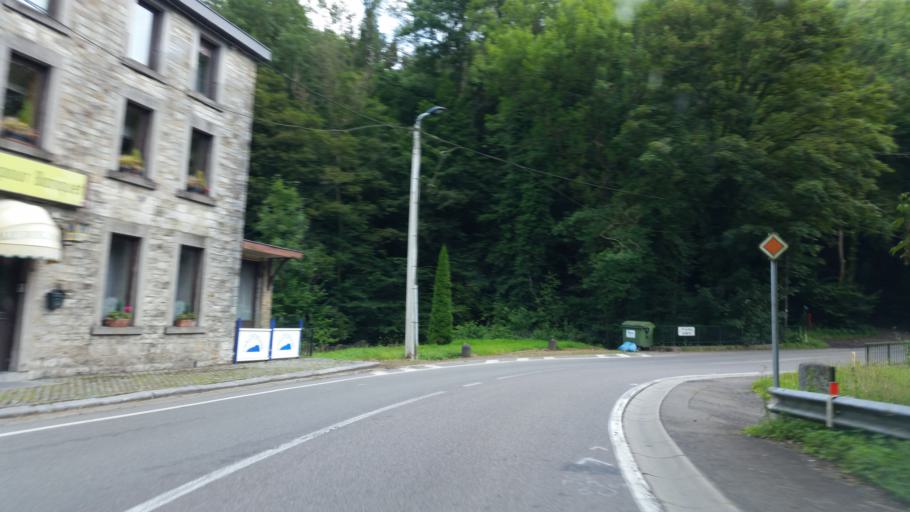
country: BE
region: Wallonia
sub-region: Province de Liege
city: Esneux
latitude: 50.5279
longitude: 5.5302
